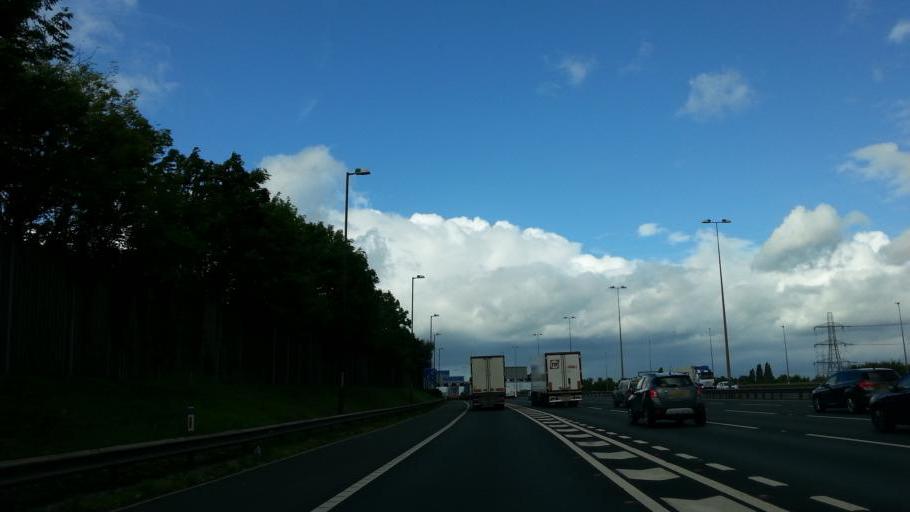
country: GB
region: England
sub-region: Warwickshire
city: Water Orton
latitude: 52.5147
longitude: -1.7258
